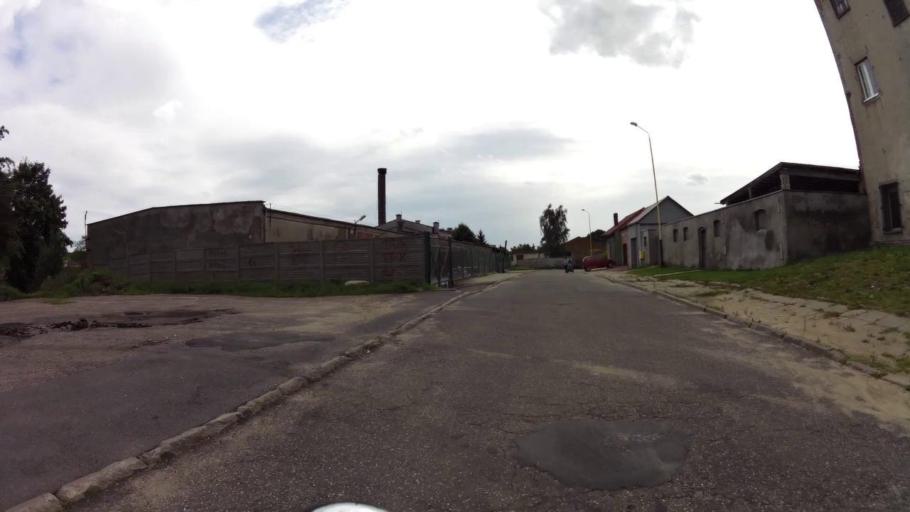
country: PL
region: West Pomeranian Voivodeship
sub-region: Powiat bialogardzki
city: Karlino
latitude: 54.0374
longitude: 15.8810
